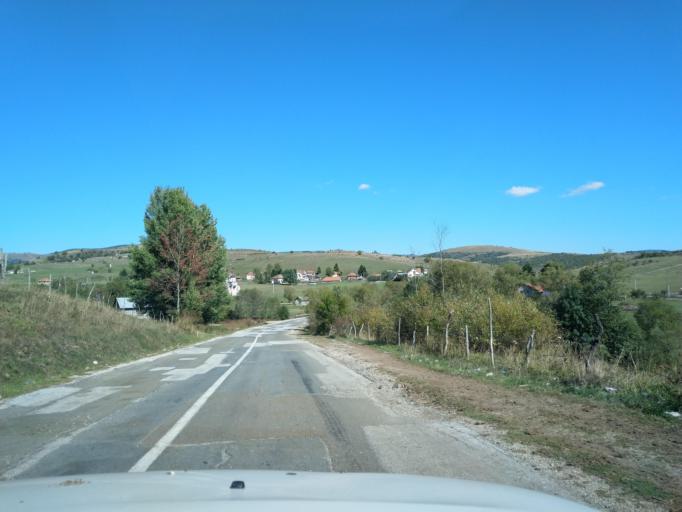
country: RS
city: Sokolovica
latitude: 43.2749
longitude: 20.1900
